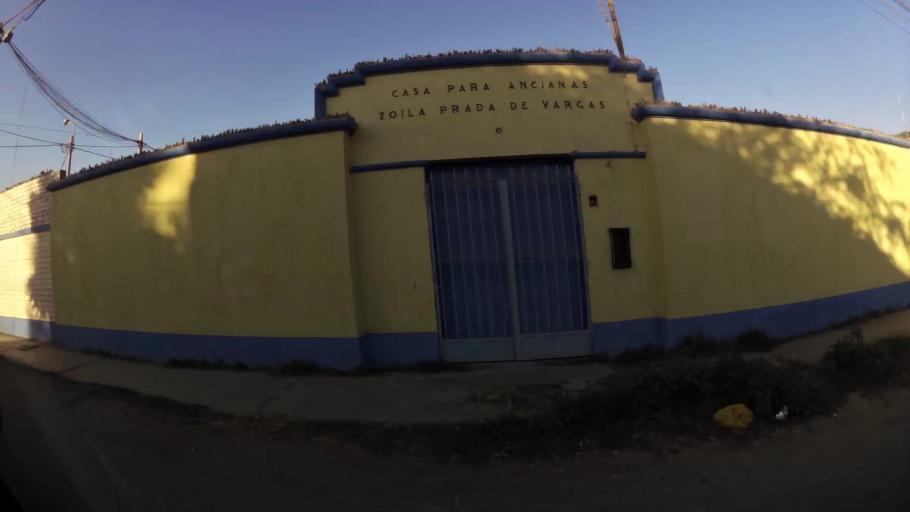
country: PE
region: Ica
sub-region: Provincia de Ica
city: Ica
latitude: -14.0579
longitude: -75.7305
